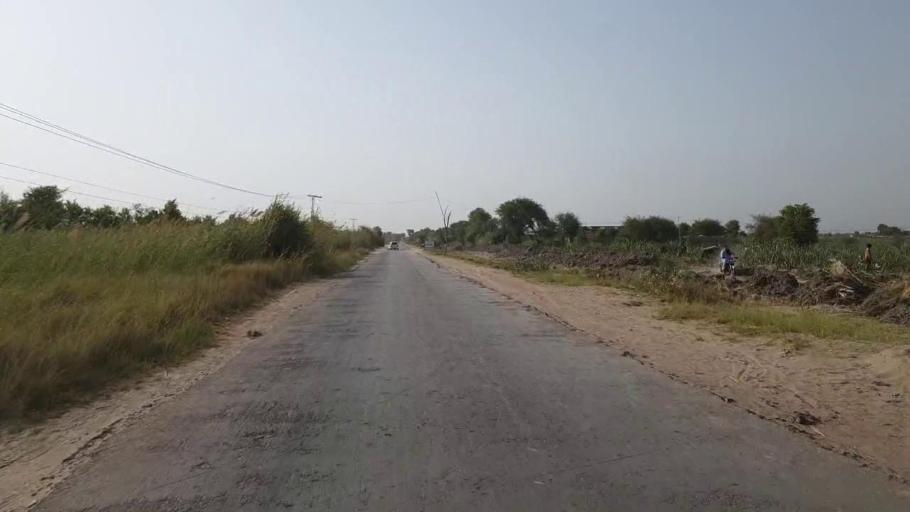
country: PK
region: Sindh
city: Sanghar
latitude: 26.2566
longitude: 68.9336
